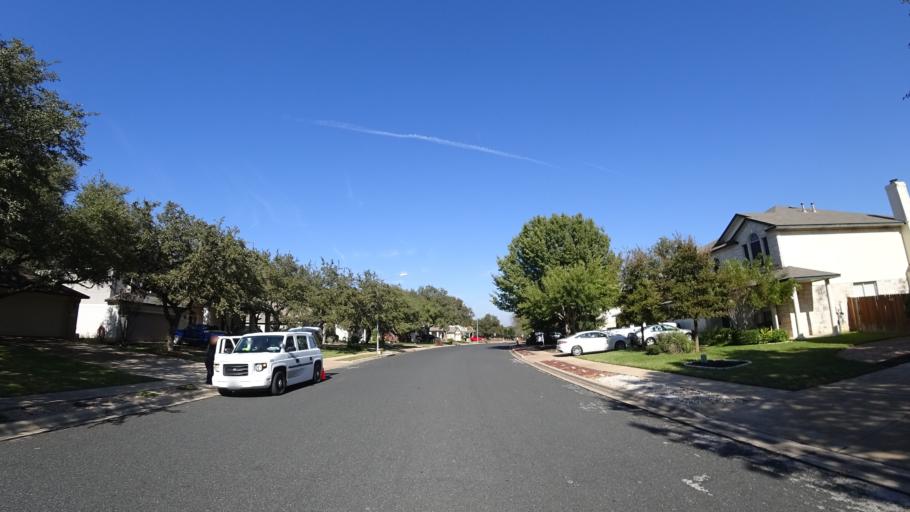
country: US
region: Texas
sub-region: Travis County
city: Shady Hollow
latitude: 30.2008
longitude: -97.8586
